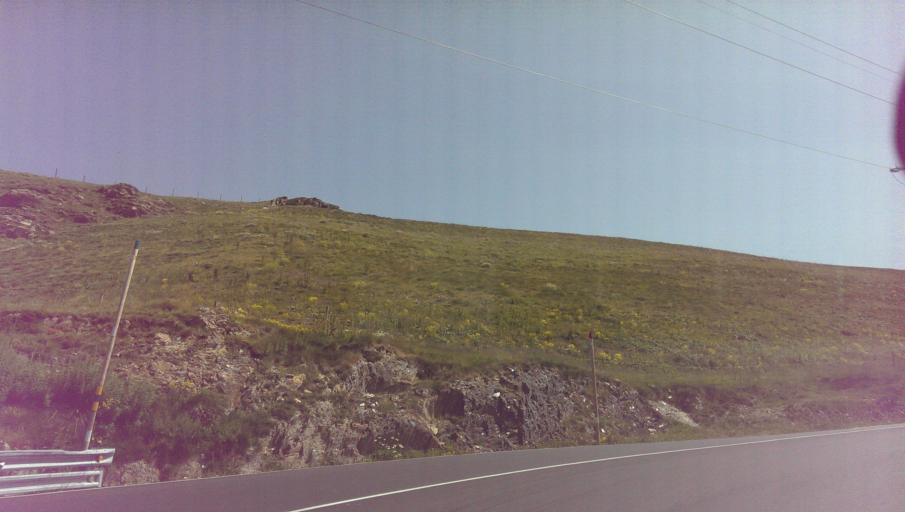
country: AD
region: Encamp
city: Pas de la Casa
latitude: 42.5424
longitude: 1.7162
